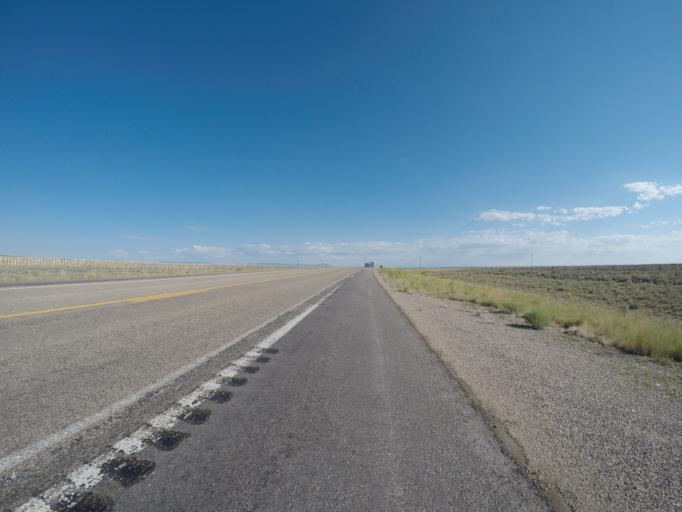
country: US
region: Wyoming
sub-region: Lincoln County
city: Kemmerer
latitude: 42.0507
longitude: -110.1625
